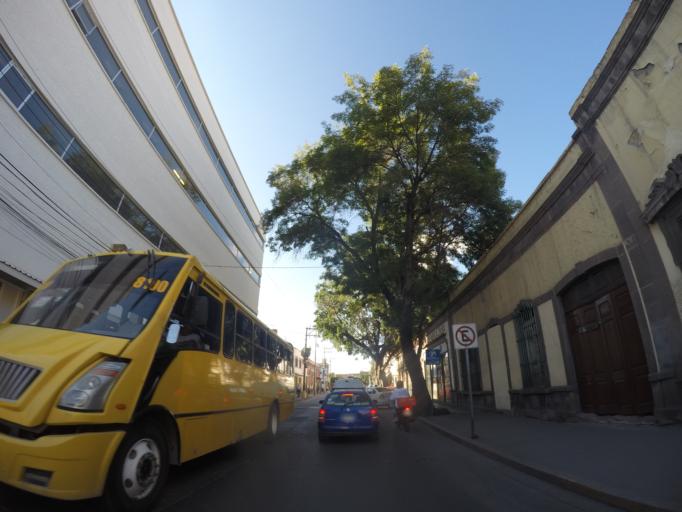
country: MX
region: San Luis Potosi
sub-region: San Luis Potosi
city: San Luis Potosi
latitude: 22.1552
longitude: -100.9793
